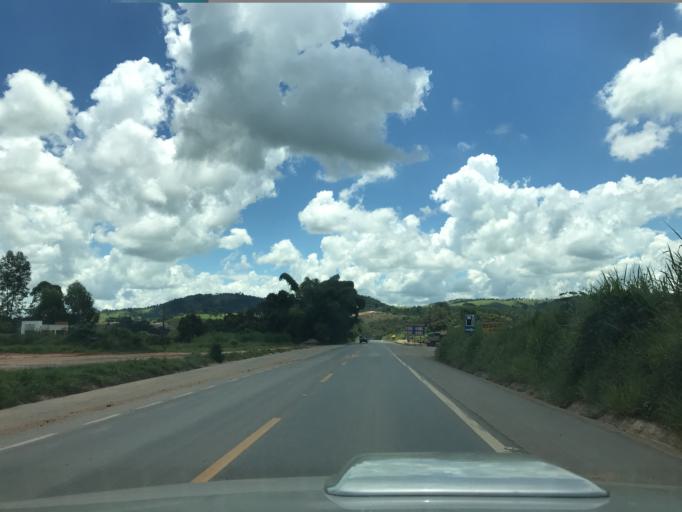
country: BR
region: Minas Gerais
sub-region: Perdoes
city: Perdoes
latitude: -21.1011
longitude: -45.0974
